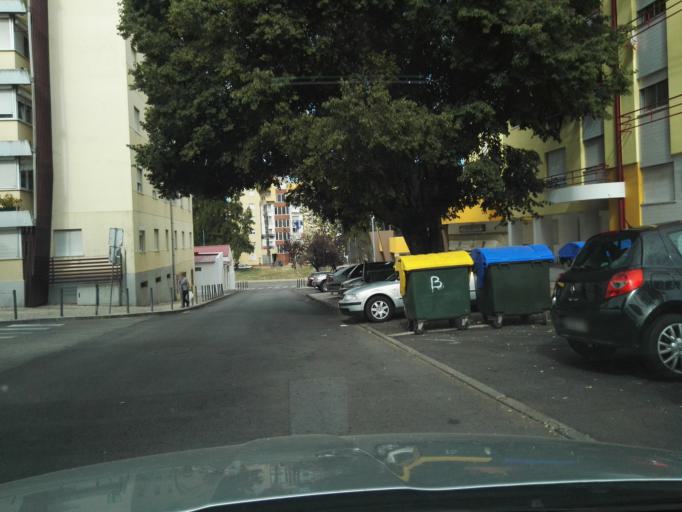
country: PT
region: Lisbon
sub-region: Amadora
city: Amadora
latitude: 38.7329
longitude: -9.2056
